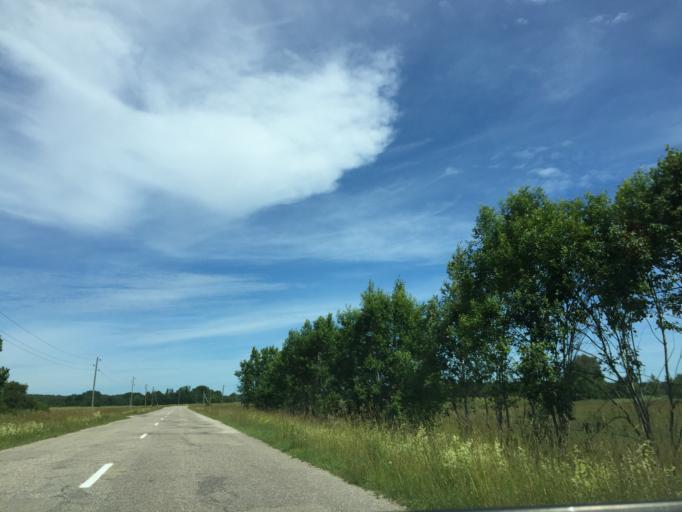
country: LV
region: Dundaga
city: Dundaga
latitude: 57.5283
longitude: 22.3300
